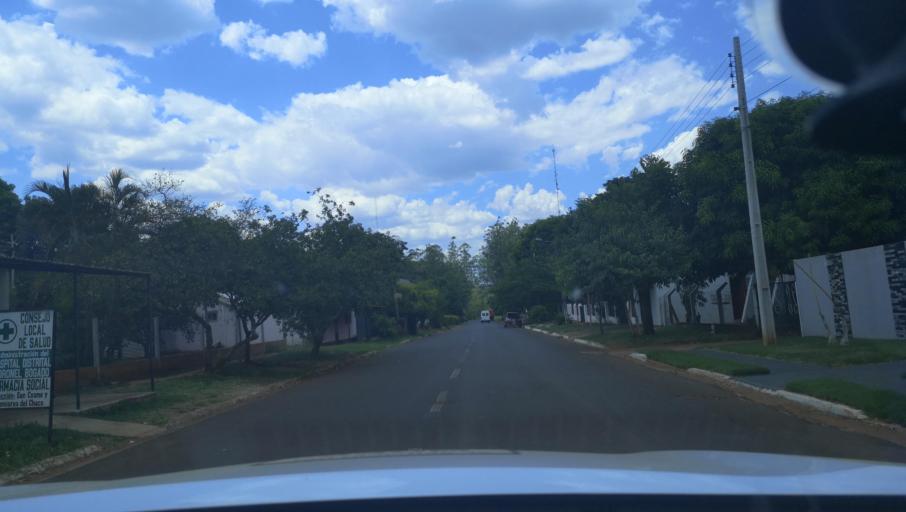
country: PY
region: Itapua
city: Carmen del Parana
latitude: -27.1703
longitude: -56.2320
